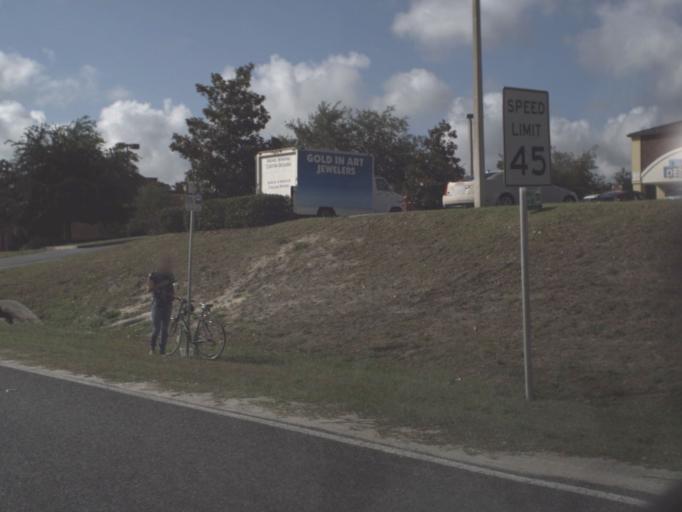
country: US
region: Florida
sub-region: Lake County
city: Lady Lake
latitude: 28.9340
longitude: -81.9361
